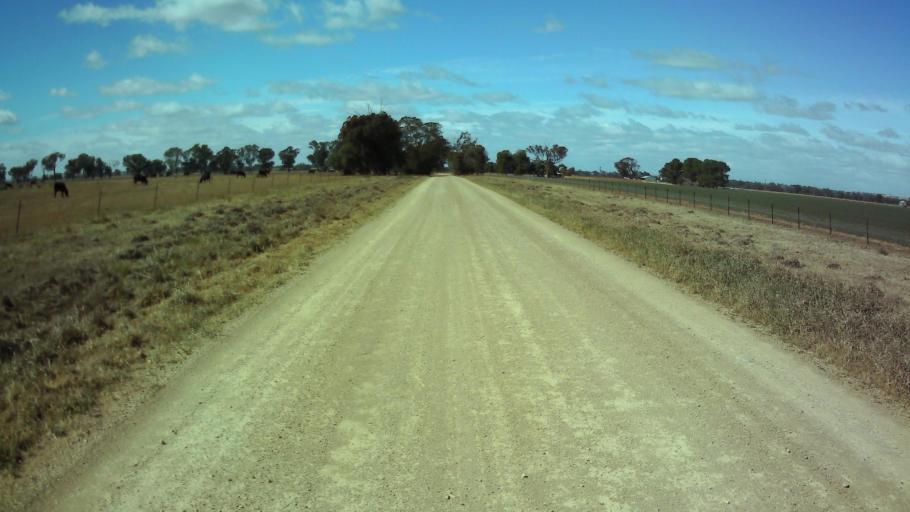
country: AU
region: New South Wales
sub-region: Weddin
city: Grenfell
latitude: -34.0250
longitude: 148.3183
